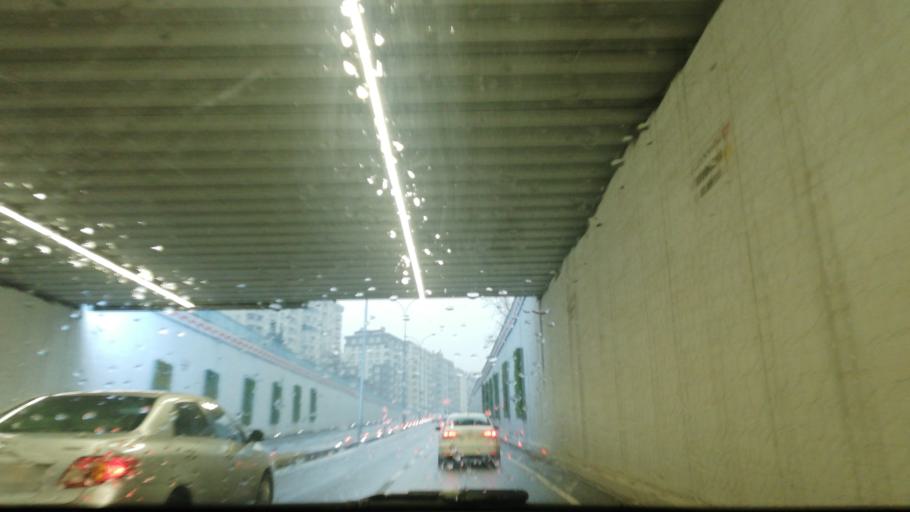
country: TR
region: Kahramanmaras
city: Kahramanmaras
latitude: 37.5844
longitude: 36.9168
